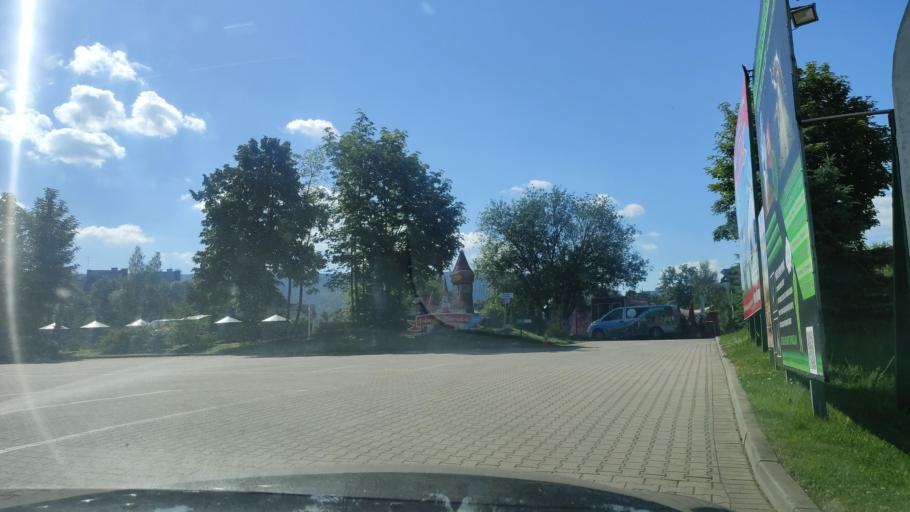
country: PL
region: Lower Silesian Voivodeship
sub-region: Powiat jeleniogorski
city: Kowary
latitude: 50.7981
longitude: 15.8340
